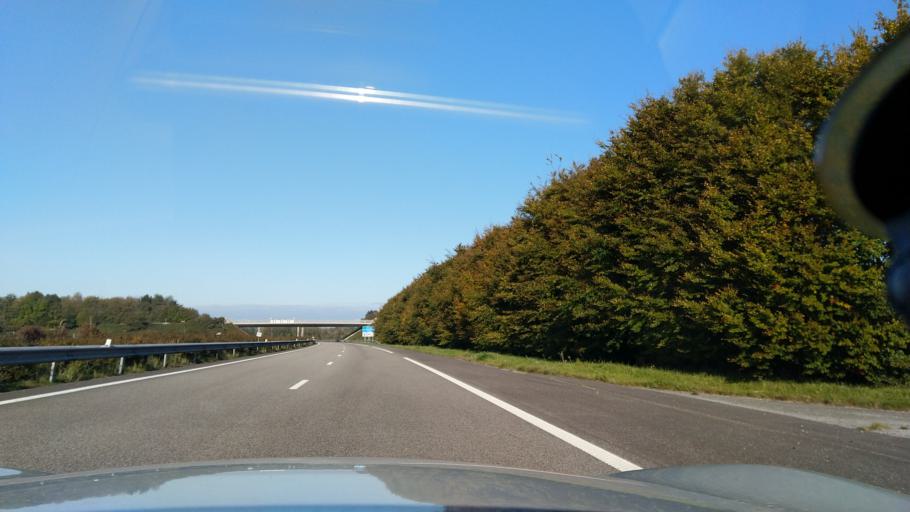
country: FR
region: Haute-Normandie
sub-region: Departement de la Seine-Maritime
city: Sainte-Marie-des-Champs
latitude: 49.6406
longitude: 0.7955
